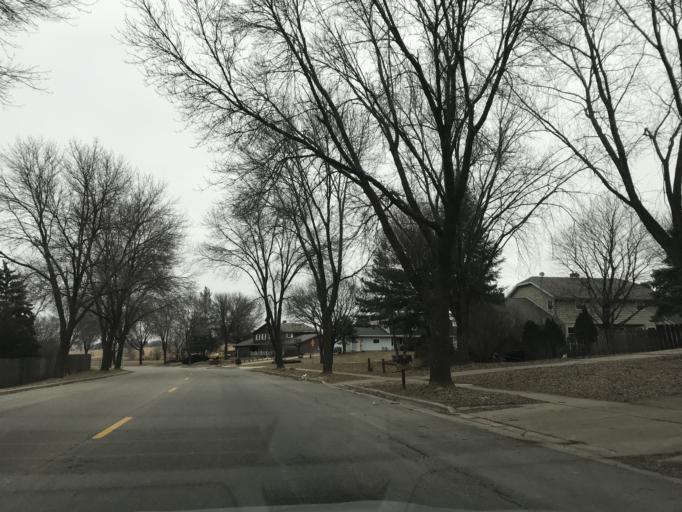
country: US
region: Wisconsin
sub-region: Dane County
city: Monona
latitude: 43.0996
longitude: -89.2887
